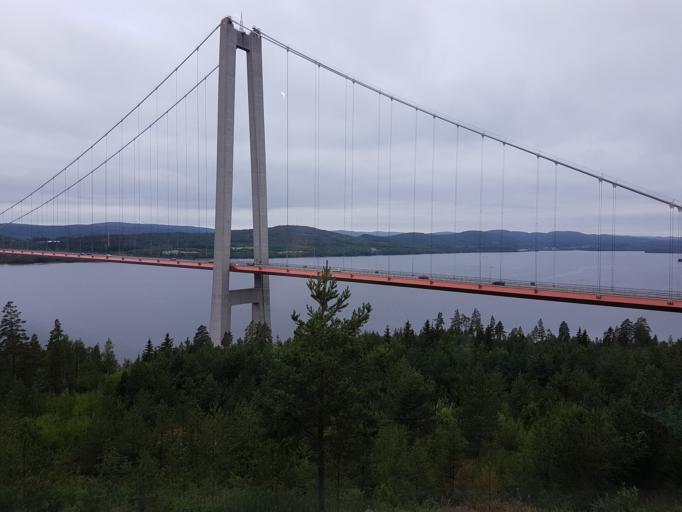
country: SE
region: Vaesternorrland
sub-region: Haernoesands Kommun
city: Haernoesand
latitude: 62.8031
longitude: 17.9517
